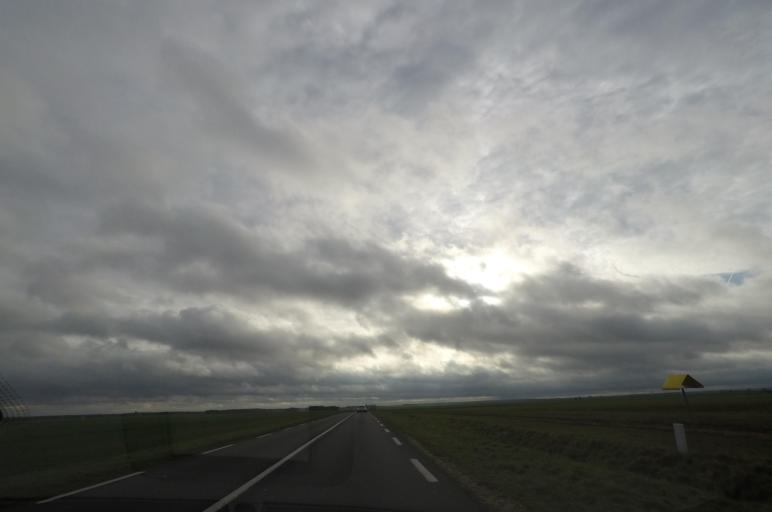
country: FR
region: Centre
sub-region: Departement du Loir-et-Cher
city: Herbault
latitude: 47.7103
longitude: 1.1656
